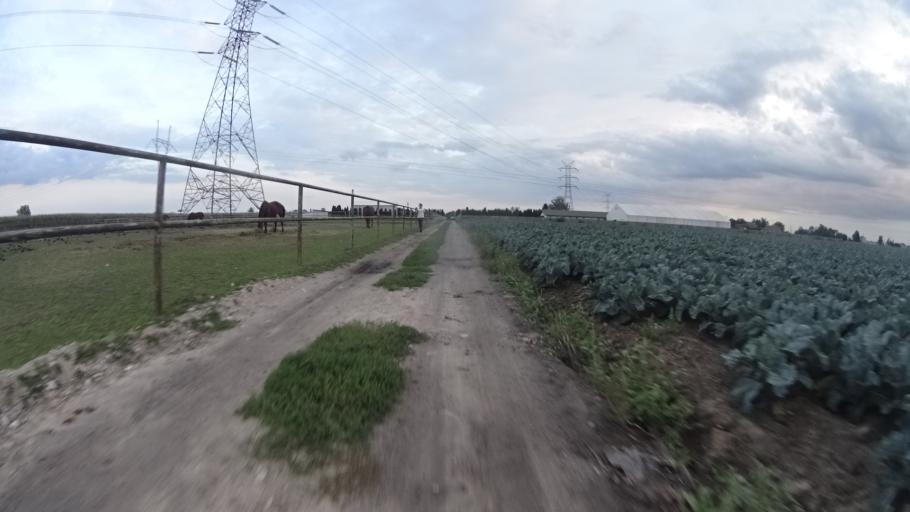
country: PL
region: Masovian Voivodeship
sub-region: Powiat warszawski zachodni
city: Ozarow Mazowiecki
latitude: 52.2382
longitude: 20.7659
